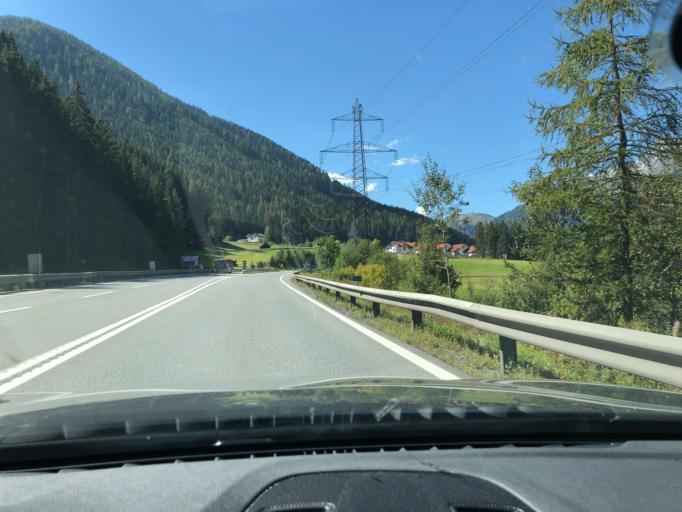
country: AT
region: Tyrol
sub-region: Politischer Bezirk Landeck
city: Flirsch
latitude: 47.1448
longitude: 10.3487
